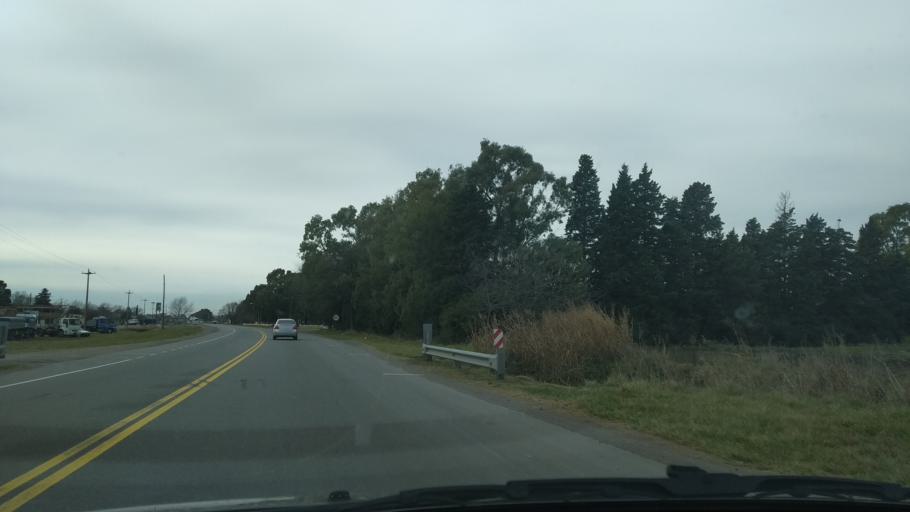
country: AR
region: Buenos Aires
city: Olavarria
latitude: -36.9835
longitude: -60.2896
